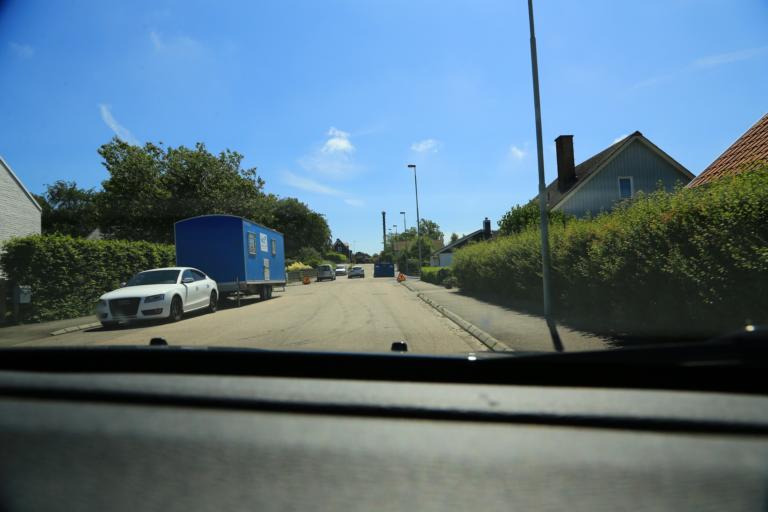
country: SE
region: Halland
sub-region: Varbergs Kommun
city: Varberg
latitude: 57.1041
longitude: 12.2757
